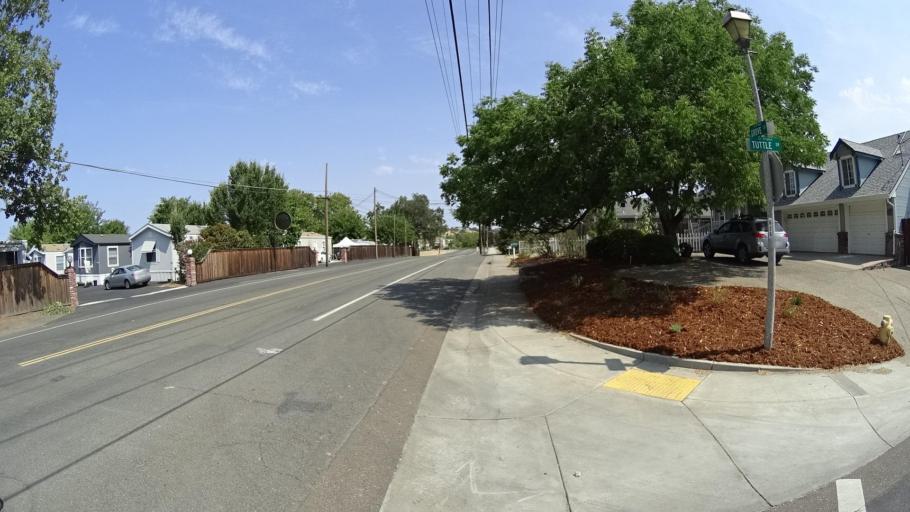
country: US
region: California
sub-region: Placer County
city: Rocklin
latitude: 38.7961
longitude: -121.2289
